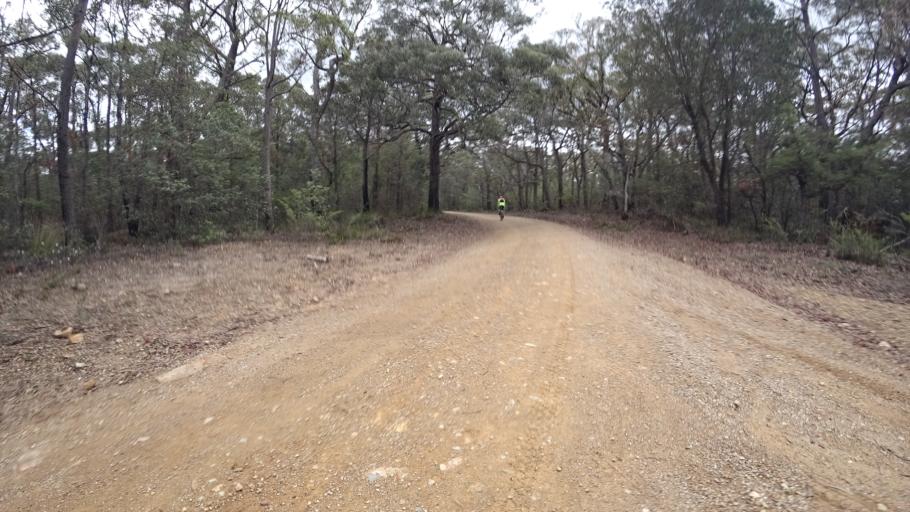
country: AU
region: New South Wales
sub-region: Shoalhaven Shire
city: Milton
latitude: -35.1629
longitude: 150.3994
